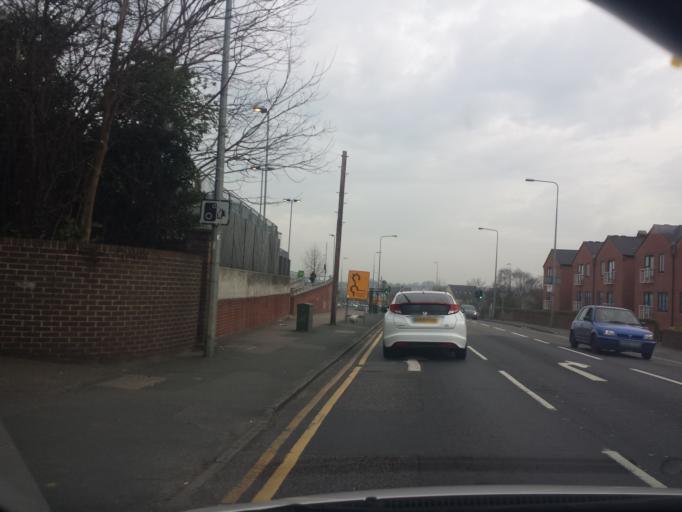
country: GB
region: England
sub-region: Essex
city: Colchester
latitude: 51.8942
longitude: 0.9181
